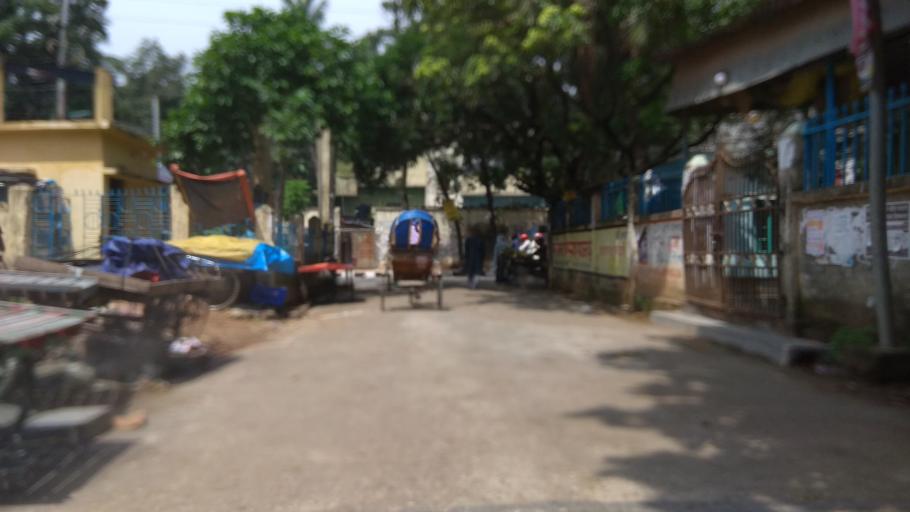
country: BD
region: Dhaka
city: Azimpur
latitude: 23.8057
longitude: 90.3604
